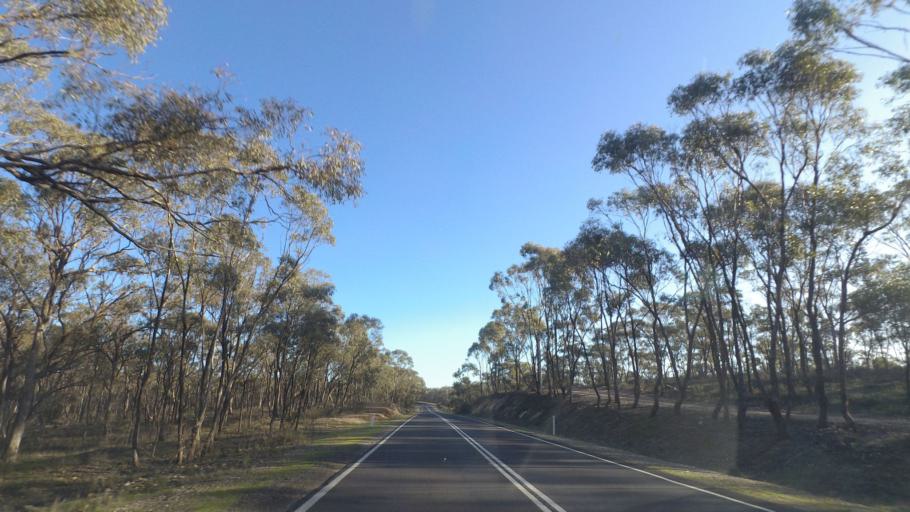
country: AU
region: Victoria
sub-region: Greater Bendigo
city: Kennington
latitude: -36.8741
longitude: 144.4969
